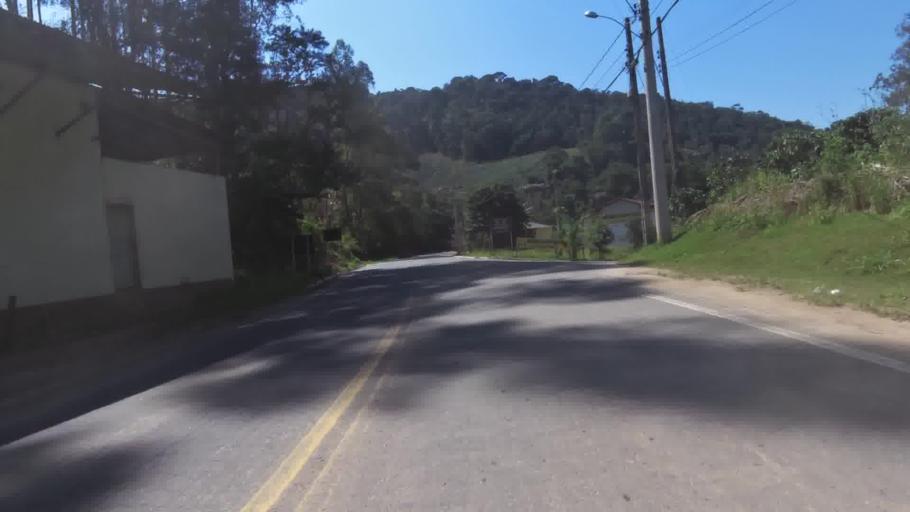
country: BR
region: Espirito Santo
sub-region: Marechal Floriano
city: Marechal Floriano
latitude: -20.4412
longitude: -40.7792
